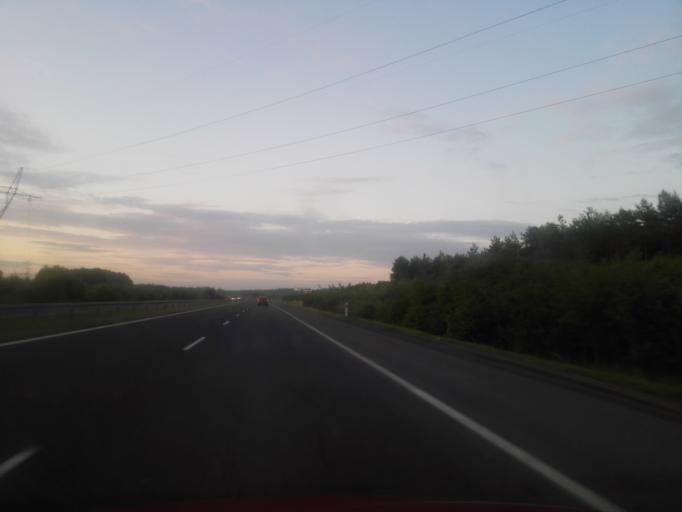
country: PL
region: Lodz Voivodeship
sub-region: Powiat radomszczanski
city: Radomsko
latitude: 51.0472
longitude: 19.3509
